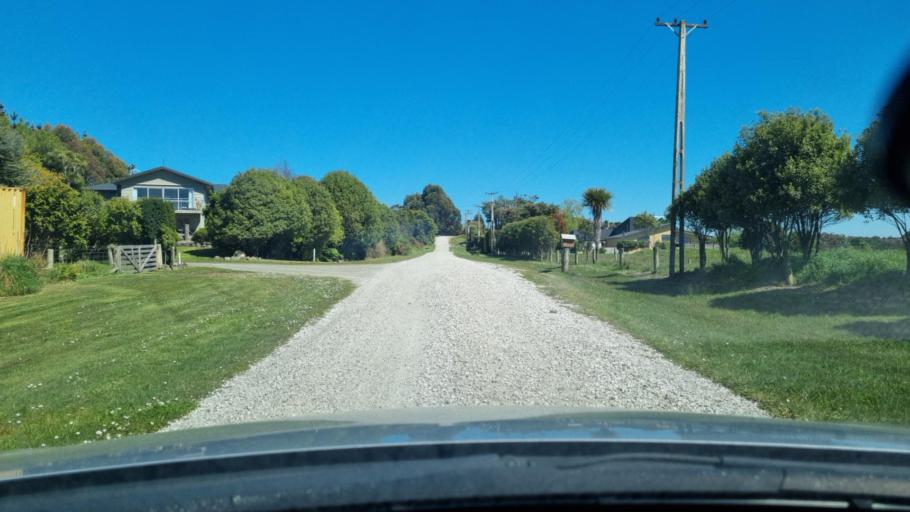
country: NZ
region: Southland
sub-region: Invercargill City
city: Invercargill
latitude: -46.4209
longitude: 168.2893
